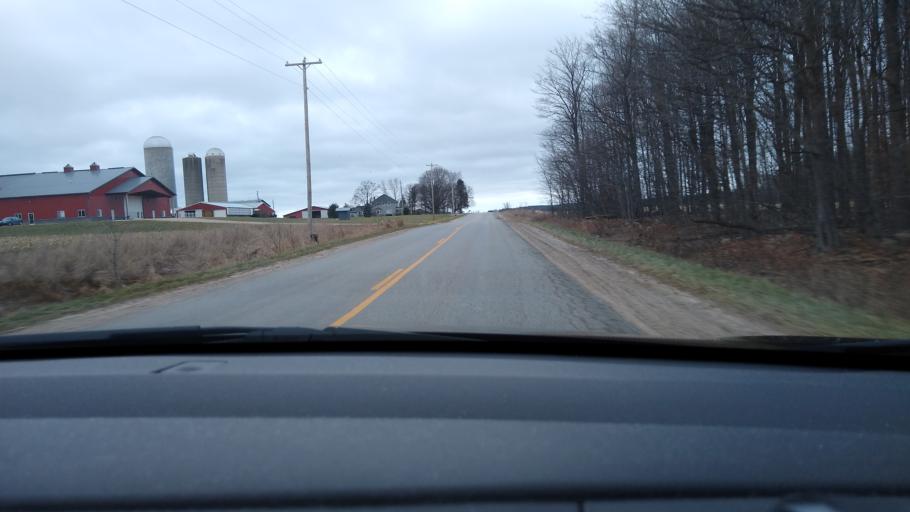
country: US
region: Michigan
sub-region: Missaukee County
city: Lake City
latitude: 44.2963
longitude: -85.0543
